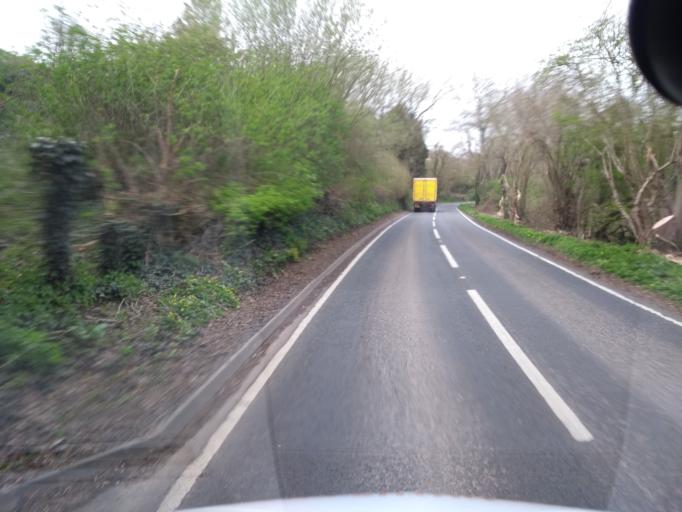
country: GB
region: England
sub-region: Somerset
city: Curry Rivel
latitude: 51.0037
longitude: -2.9438
